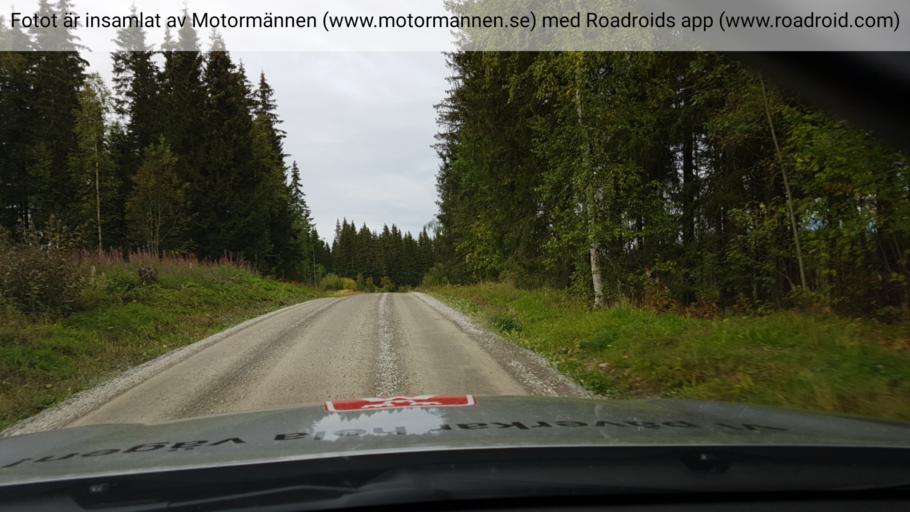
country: SE
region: Jaemtland
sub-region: Bergs Kommun
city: Hoverberg
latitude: 62.9216
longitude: 14.3050
